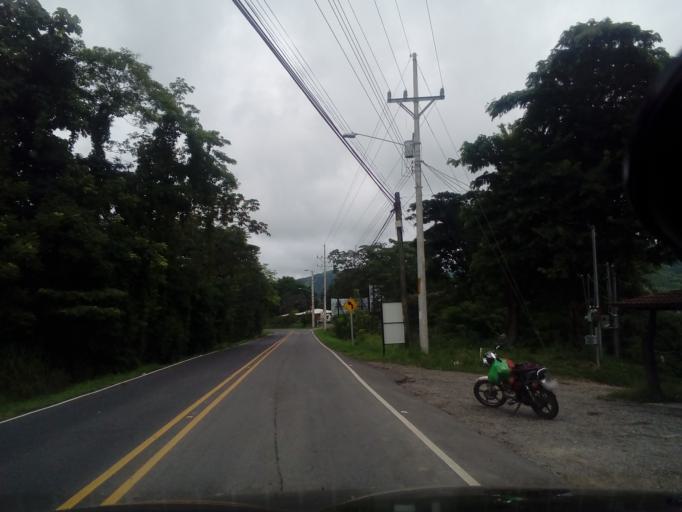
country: CR
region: Guanacaste
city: Samara
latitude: 9.9212
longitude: -85.5234
